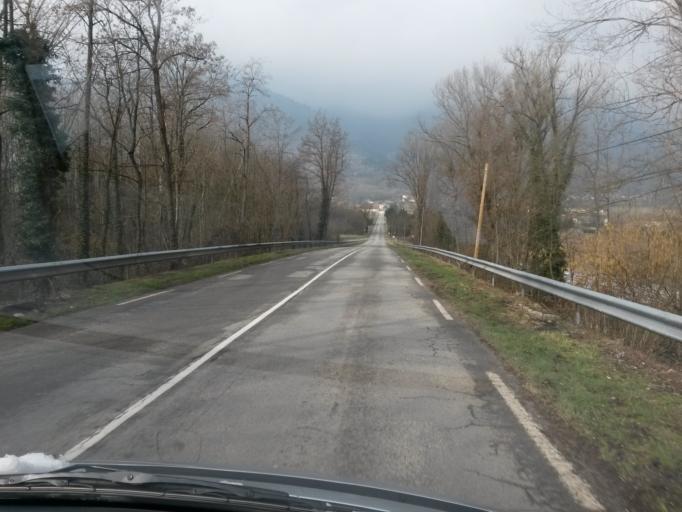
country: FR
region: Rhone-Alpes
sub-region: Departement de l'Isere
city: La Terrasse
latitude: 45.3182
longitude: 5.9418
